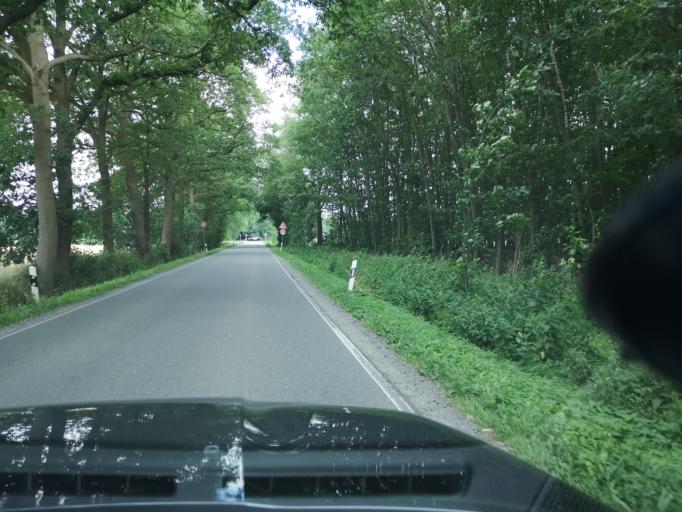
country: DE
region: North Rhine-Westphalia
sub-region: Regierungsbezirk Munster
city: Rhede
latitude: 51.8888
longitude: 6.6831
